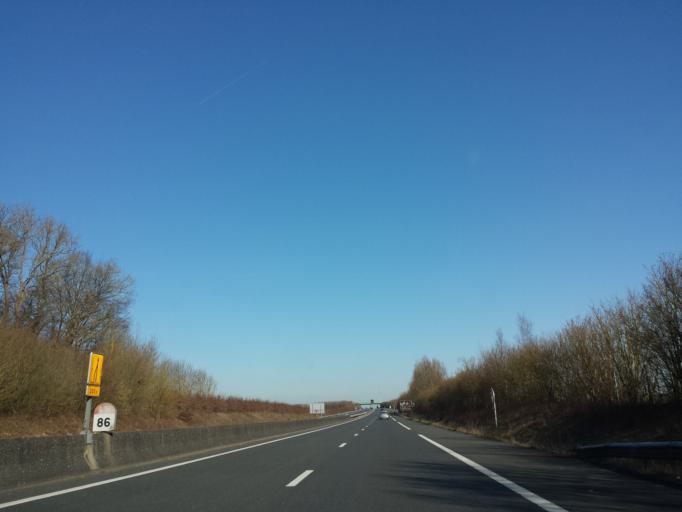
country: FR
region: Picardie
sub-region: Departement de l'Oise
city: Tille
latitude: 49.5481
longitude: 2.1892
